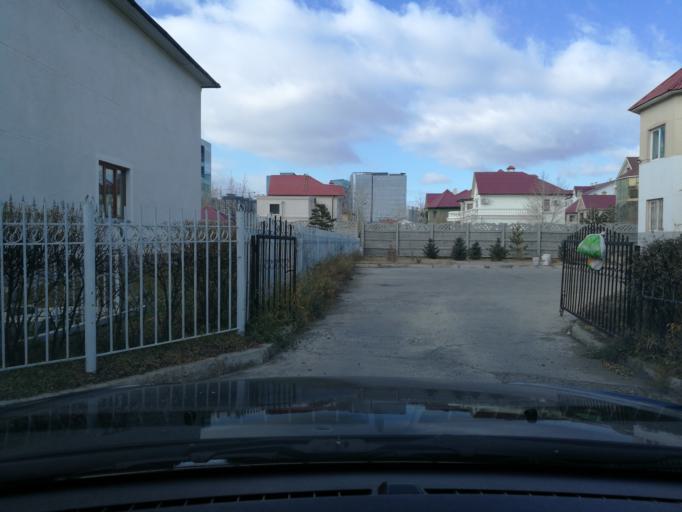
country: MN
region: Ulaanbaatar
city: Ulaanbaatar
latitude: 47.9050
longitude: 106.9249
